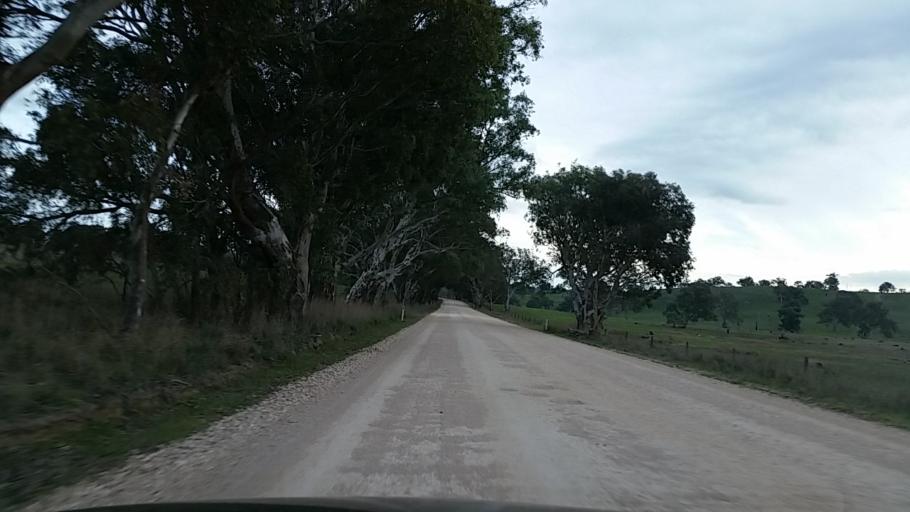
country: AU
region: South Australia
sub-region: Adelaide Hills
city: Birdwood
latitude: -34.8799
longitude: 139.0237
